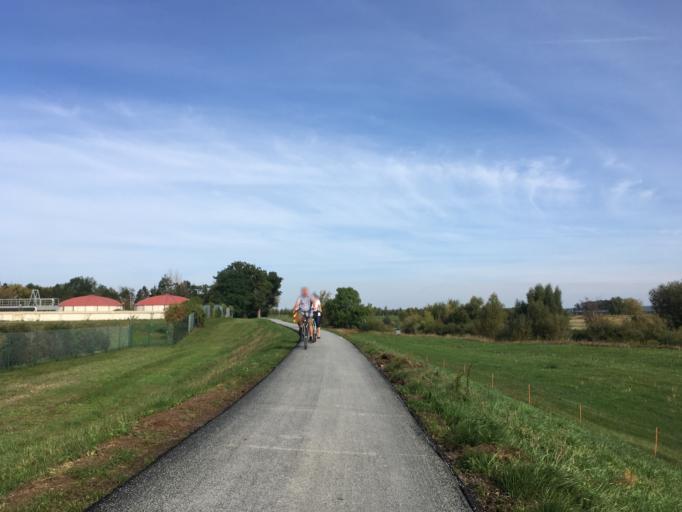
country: DE
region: Brandenburg
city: Forst
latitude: 51.7600
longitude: 14.6512
